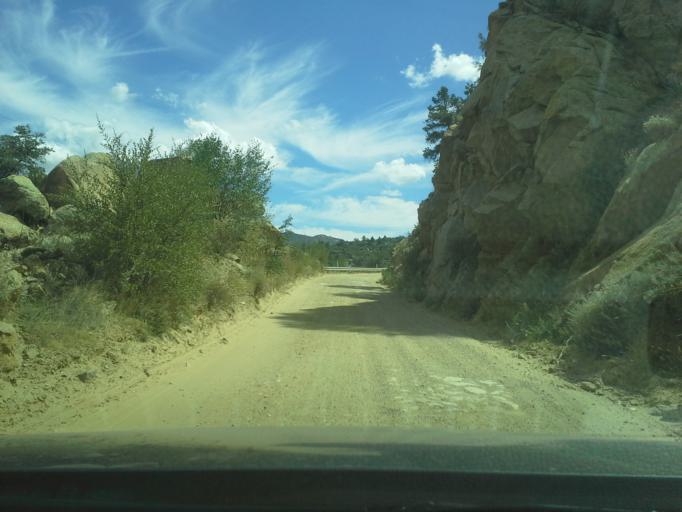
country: US
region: Arizona
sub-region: Yavapai County
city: Mayer
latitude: 34.2387
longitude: -112.3030
